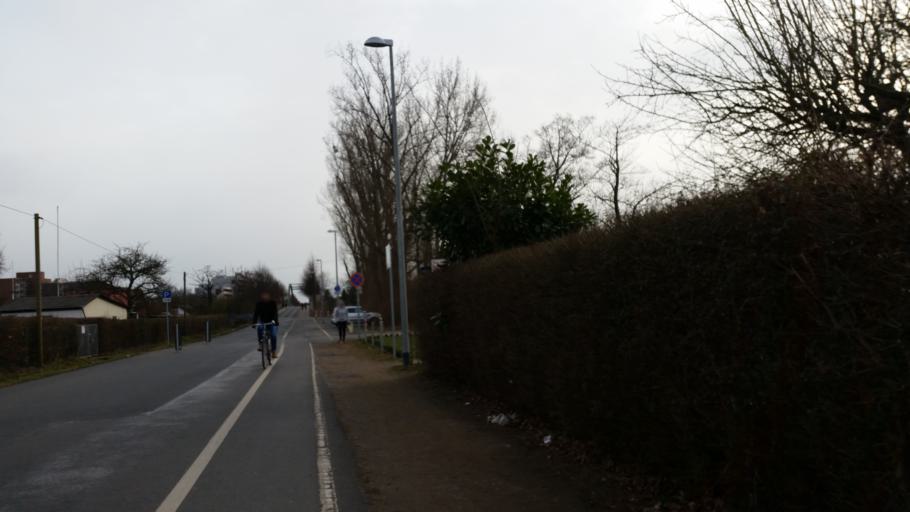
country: DE
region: Lower Saxony
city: Langenhagen
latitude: 52.4089
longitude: 9.7736
